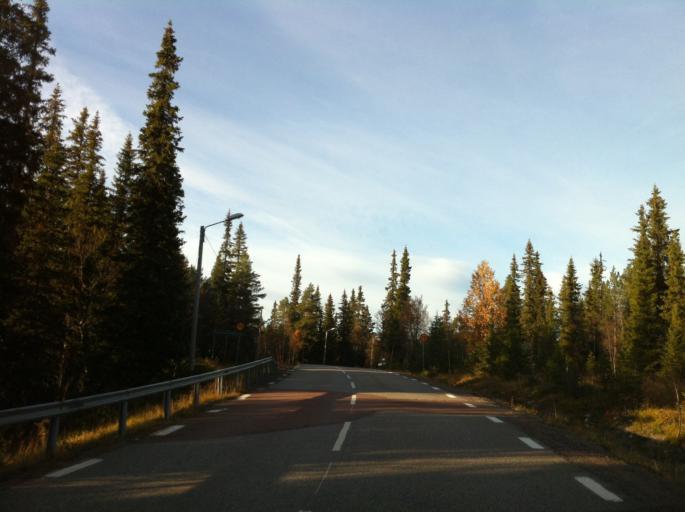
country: NO
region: Hedmark
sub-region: Engerdal
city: Engerdal
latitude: 62.0698
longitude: 12.3126
